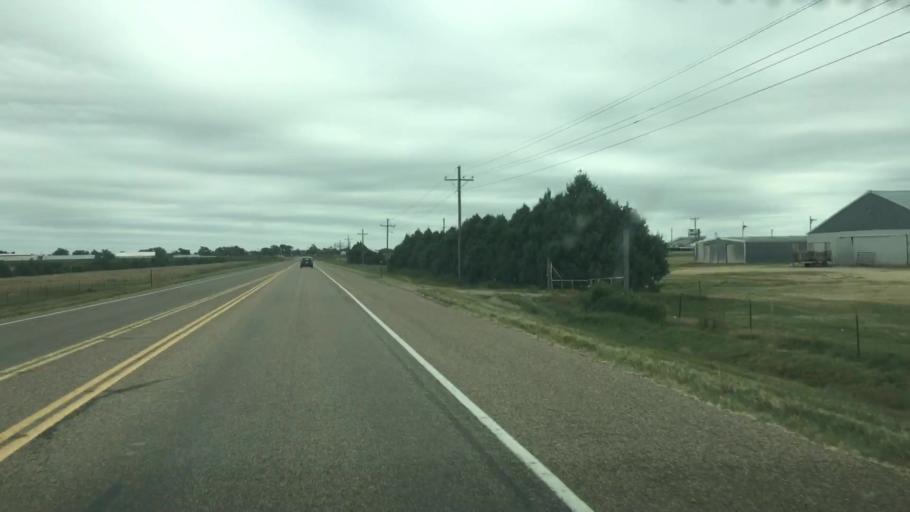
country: US
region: Kansas
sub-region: Hamilton County
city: Syracuse
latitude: 38.0547
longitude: -102.1507
